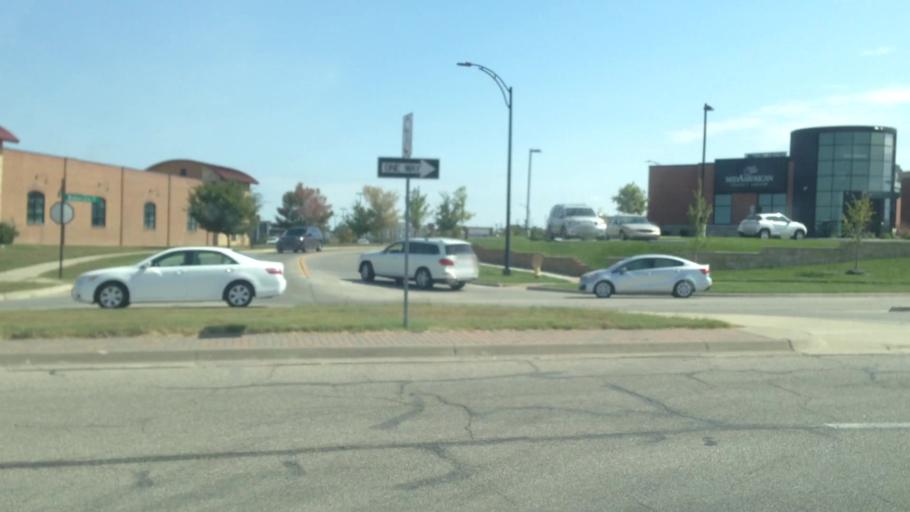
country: US
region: Kansas
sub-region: Douglas County
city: Lawrence
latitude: 38.9728
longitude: -95.3071
